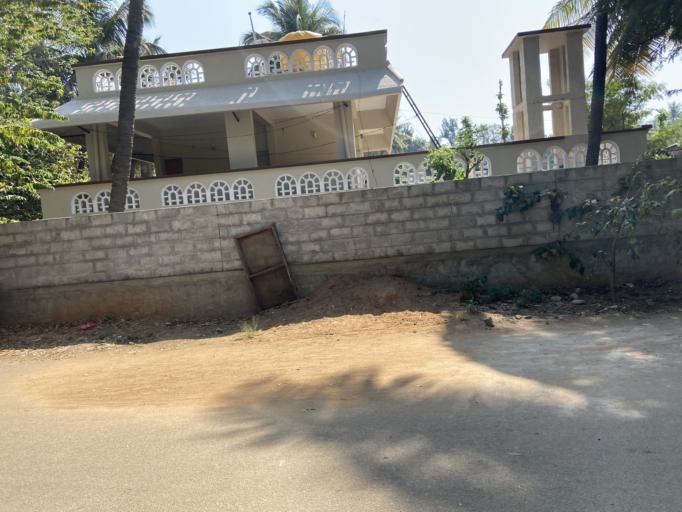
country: IN
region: Karnataka
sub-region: Bangalore Urban
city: Bangalore
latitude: 12.9458
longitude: 77.6759
